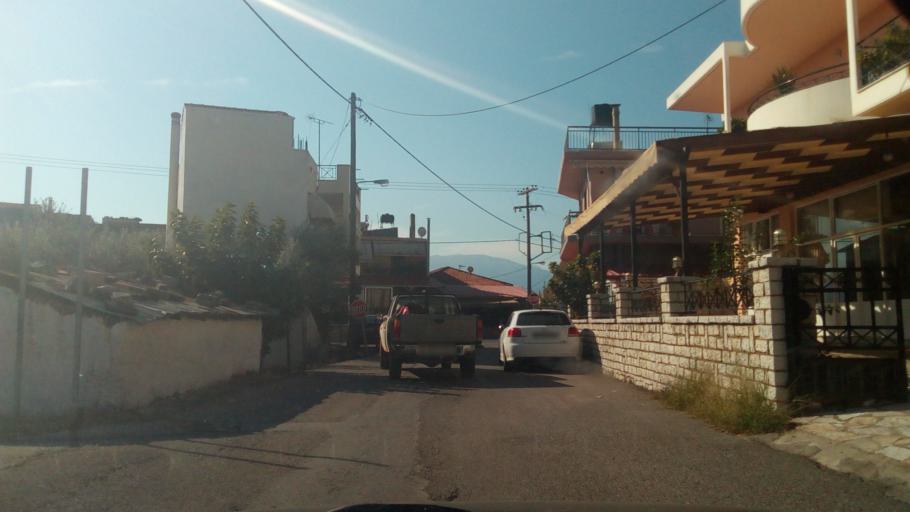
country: GR
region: West Greece
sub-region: Nomos Aitolias kai Akarnanias
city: Nafpaktos
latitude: 38.4021
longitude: 21.8560
